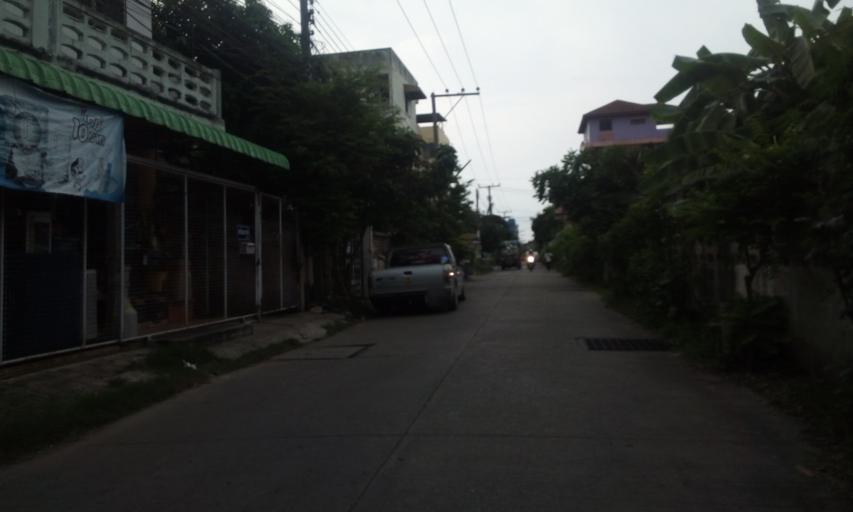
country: TH
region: Bangkok
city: Sai Mai
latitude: 13.9814
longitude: 100.6236
